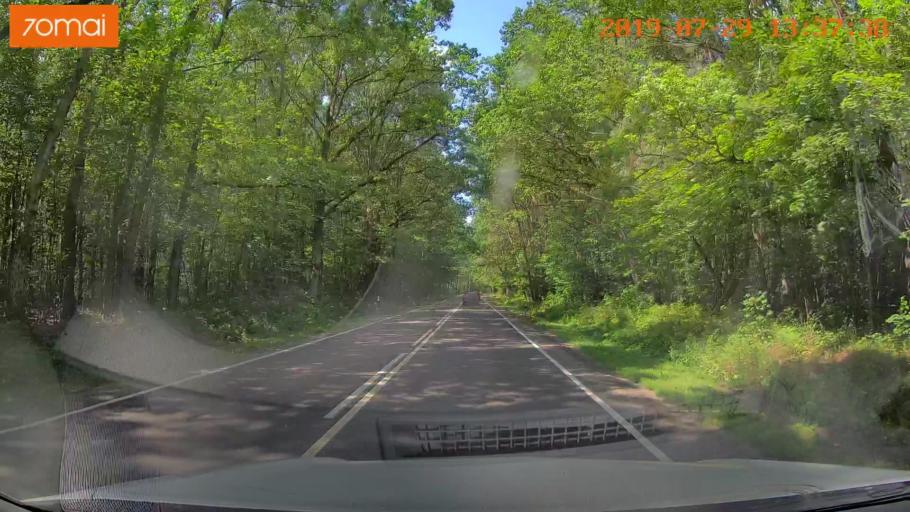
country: RU
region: Kaliningrad
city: Volochayevskoye
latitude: 54.7156
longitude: 20.1814
